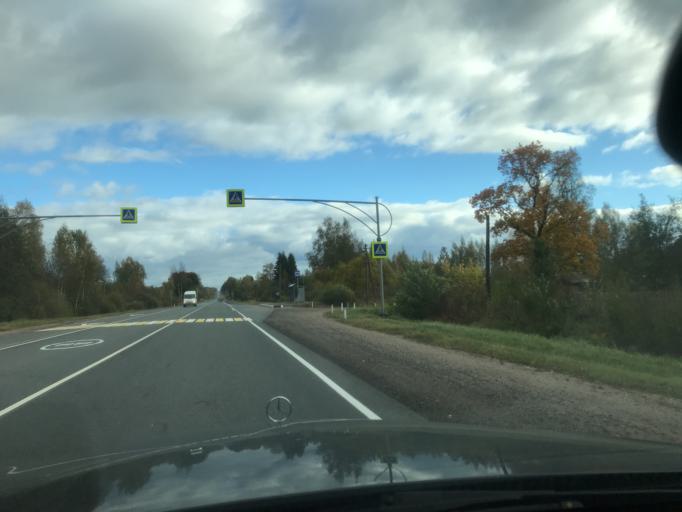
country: RU
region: Pskov
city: Opochka
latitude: 56.6726
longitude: 28.7249
